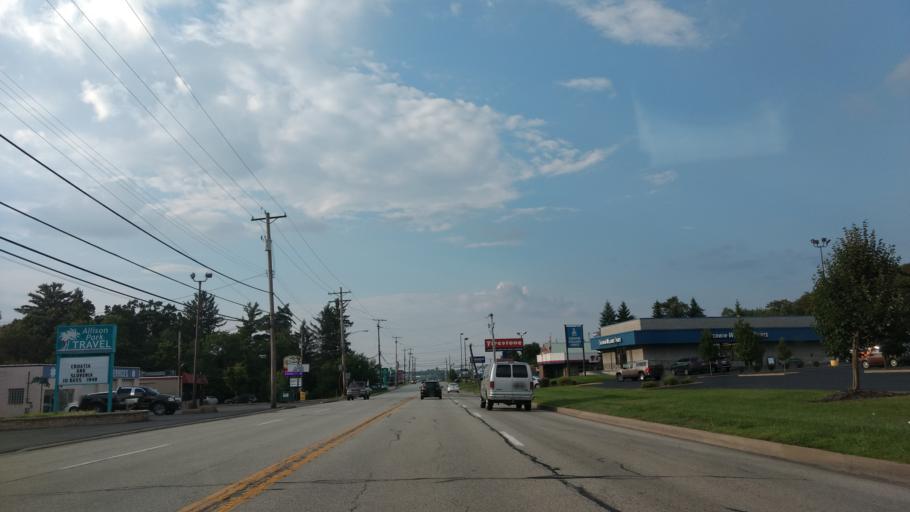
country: US
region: Pennsylvania
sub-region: Allegheny County
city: Allison Park
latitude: 40.5937
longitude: -79.9478
